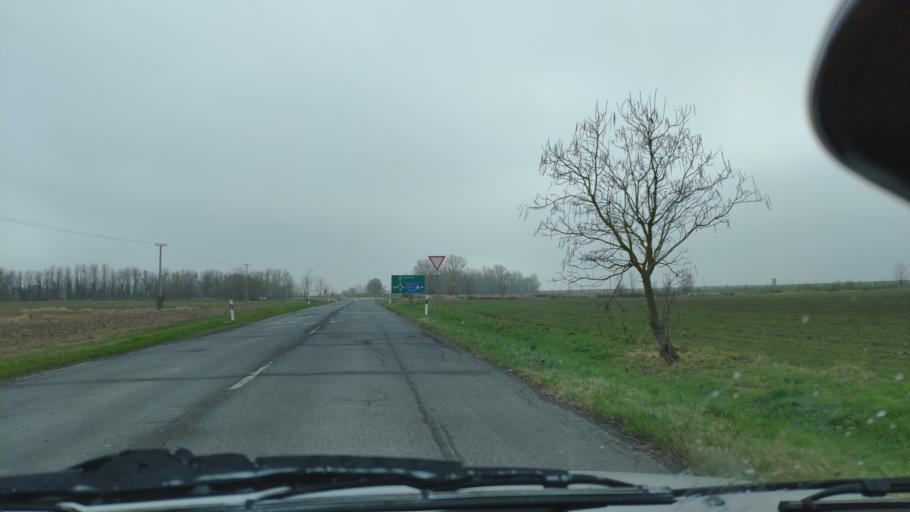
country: HU
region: Zala
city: Zalakomar
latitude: 46.5894
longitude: 17.2634
